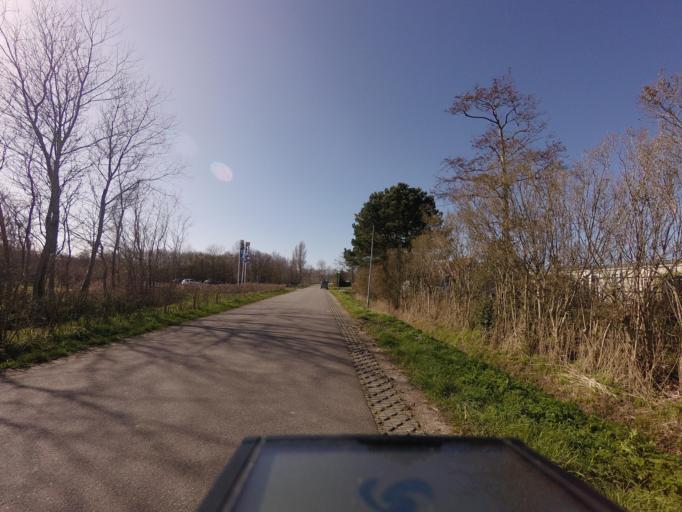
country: NL
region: Zeeland
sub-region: Schouwen-Duiveland
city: Renesse
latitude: 51.7384
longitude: 3.7872
